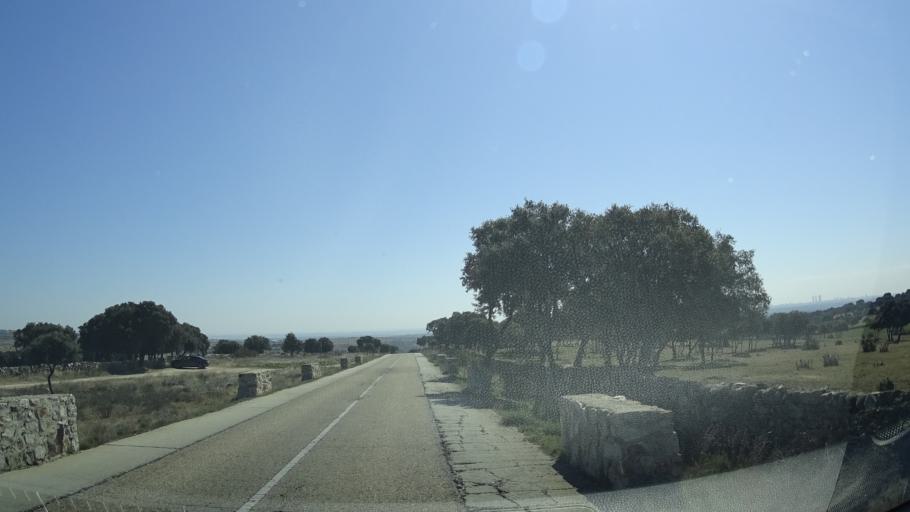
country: ES
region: Madrid
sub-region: Provincia de Madrid
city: Colmenar Viejo
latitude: 40.6458
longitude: -3.8235
